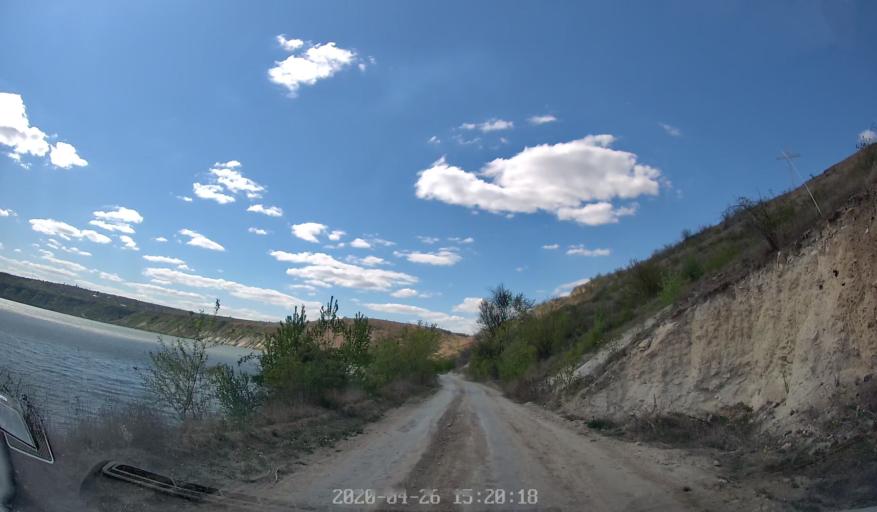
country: MD
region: Telenesti
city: Cocieri
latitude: 47.3637
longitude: 29.0969
